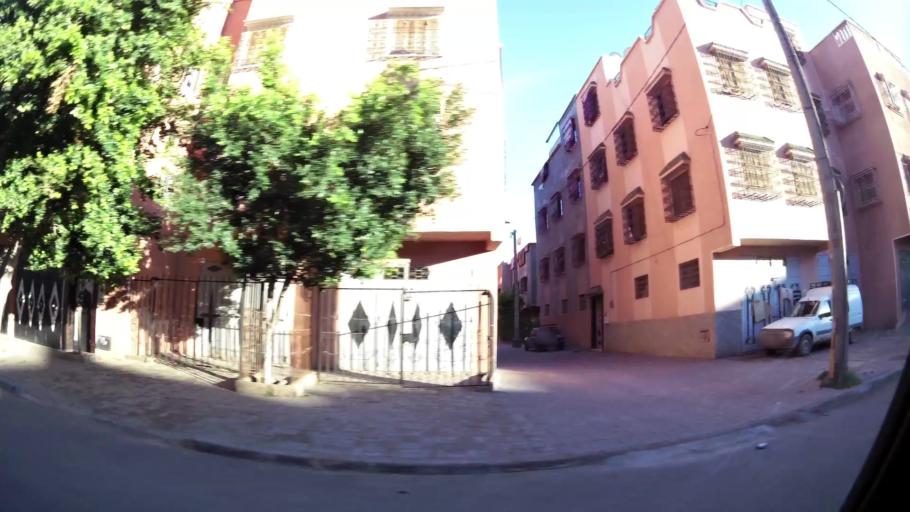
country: MA
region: Marrakech-Tensift-Al Haouz
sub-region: Marrakech
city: Marrakesh
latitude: 31.6171
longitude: -8.0536
